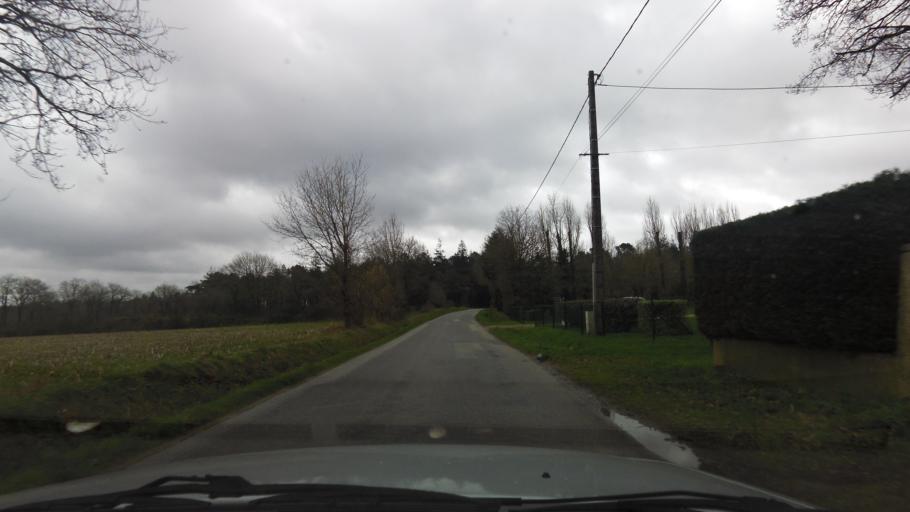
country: FR
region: Brittany
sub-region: Departement du Morbihan
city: Elven
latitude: 47.7943
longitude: -2.5789
